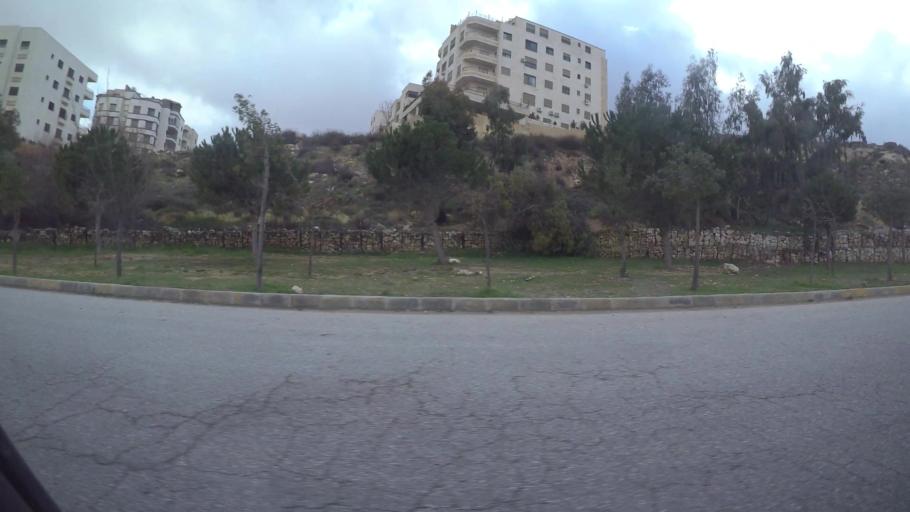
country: JO
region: Amman
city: Al Jubayhah
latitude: 32.0428
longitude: 35.8740
